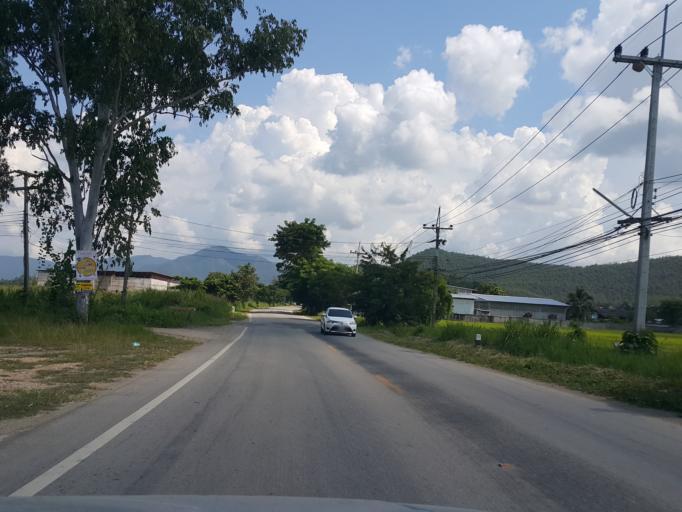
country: TH
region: Chiang Mai
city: San Kamphaeng
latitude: 18.7215
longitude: 99.1752
